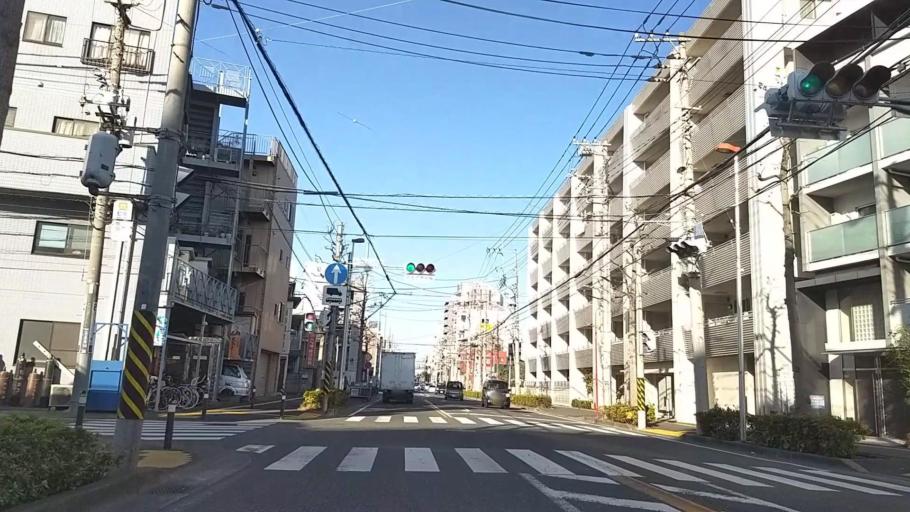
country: JP
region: Tokyo
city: Chofugaoka
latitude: 35.6014
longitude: 139.6205
